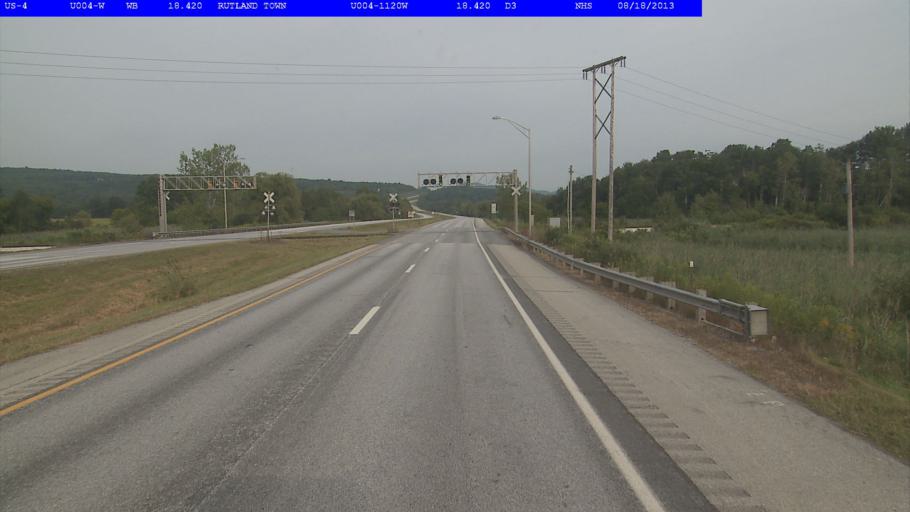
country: US
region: Vermont
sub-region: Rutland County
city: Rutland
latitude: 43.5807
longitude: -72.9743
